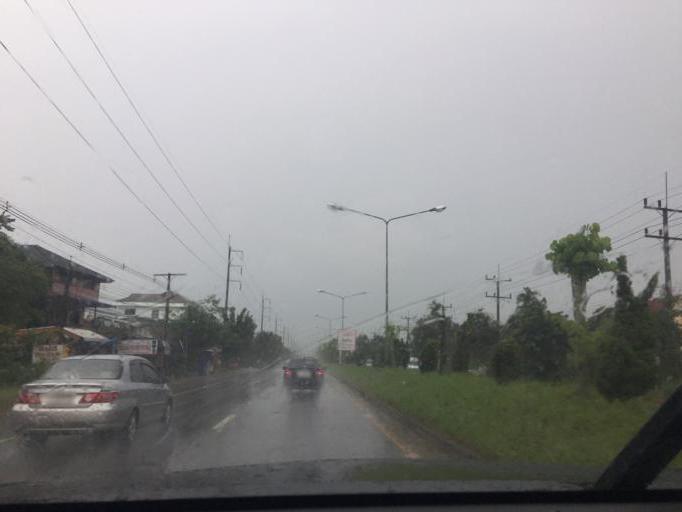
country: TH
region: Chiang Rai
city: Mae Fa Luang
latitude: 20.2536
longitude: 99.8560
